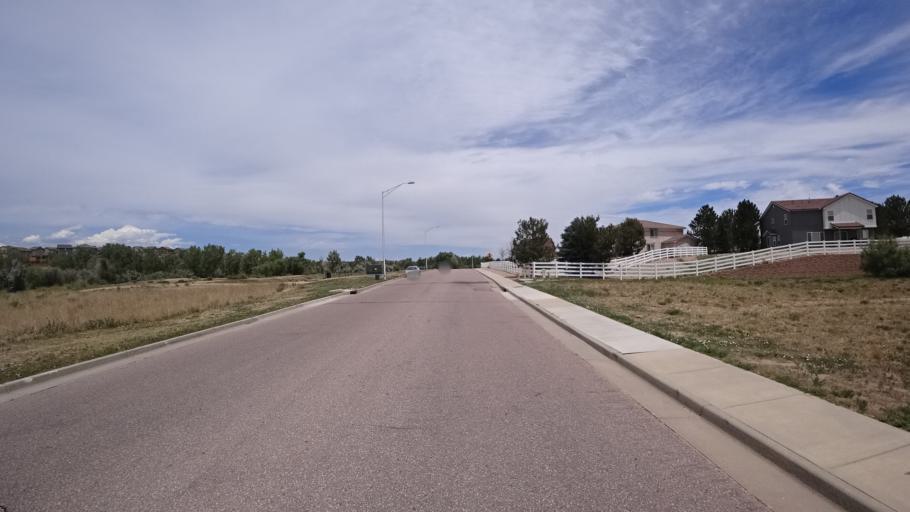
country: US
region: Colorado
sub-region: El Paso County
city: Fountain
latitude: 38.6901
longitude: -104.6851
